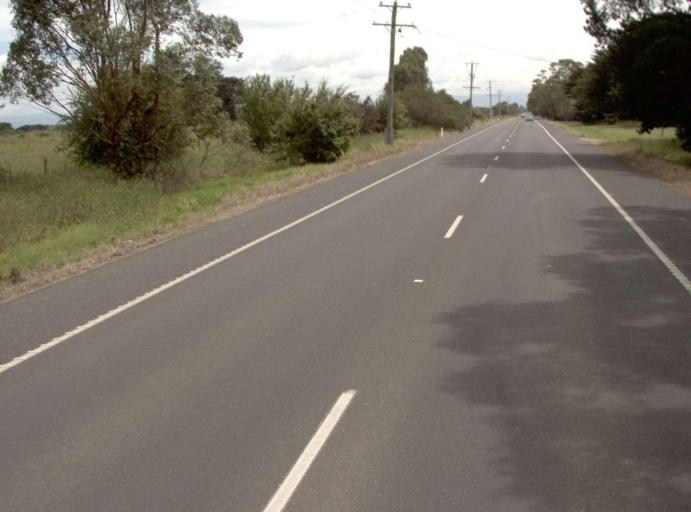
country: AU
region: Victoria
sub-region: Wellington
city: Sale
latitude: -38.0404
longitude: 147.0189
